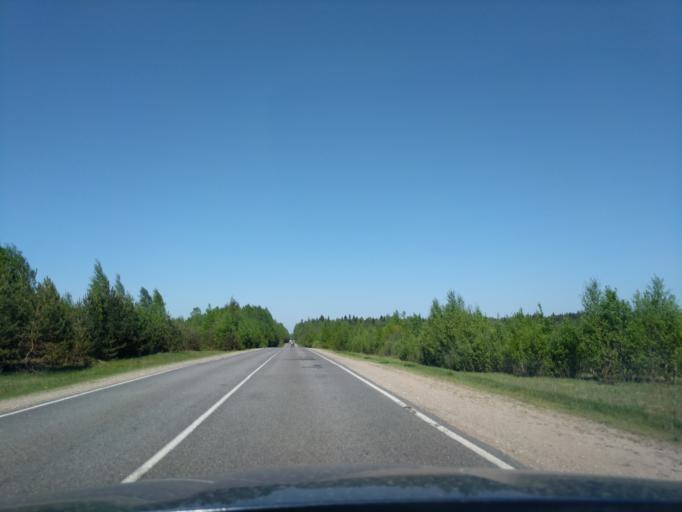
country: BY
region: Minsk
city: Il'ya
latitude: 54.3988
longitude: 27.3323
